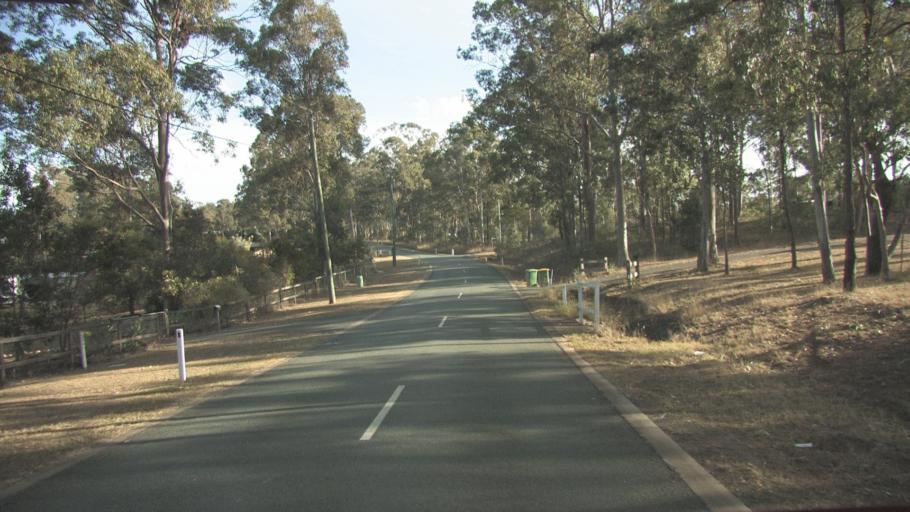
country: AU
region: Queensland
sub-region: Logan
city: Cedar Vale
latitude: -27.8849
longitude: 153.0083
